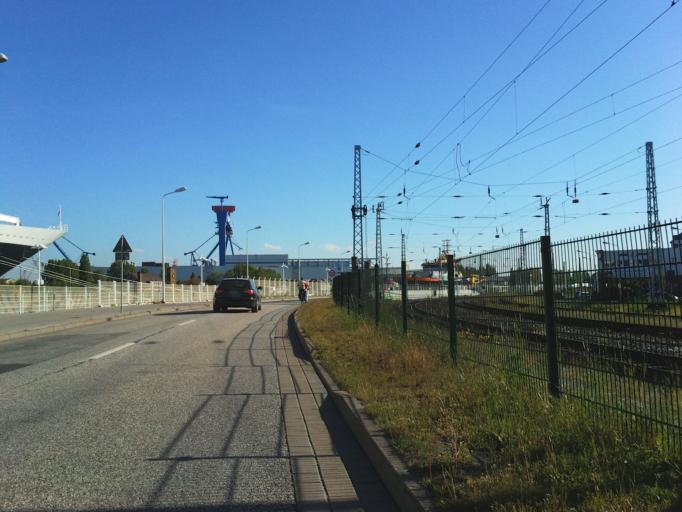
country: DE
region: Mecklenburg-Vorpommern
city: Warnemuende
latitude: 54.1736
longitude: 12.0927
